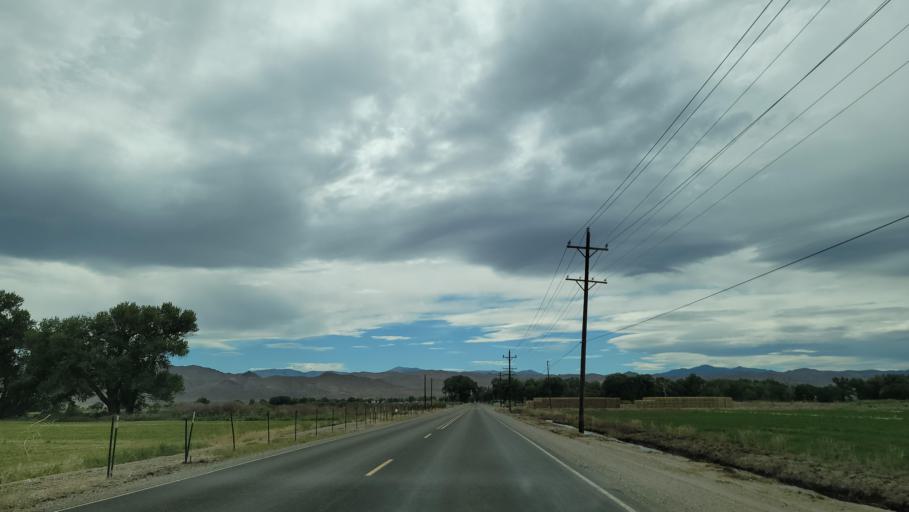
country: US
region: Nevada
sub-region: Lyon County
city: Yerington
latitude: 39.0481
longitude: -119.1703
